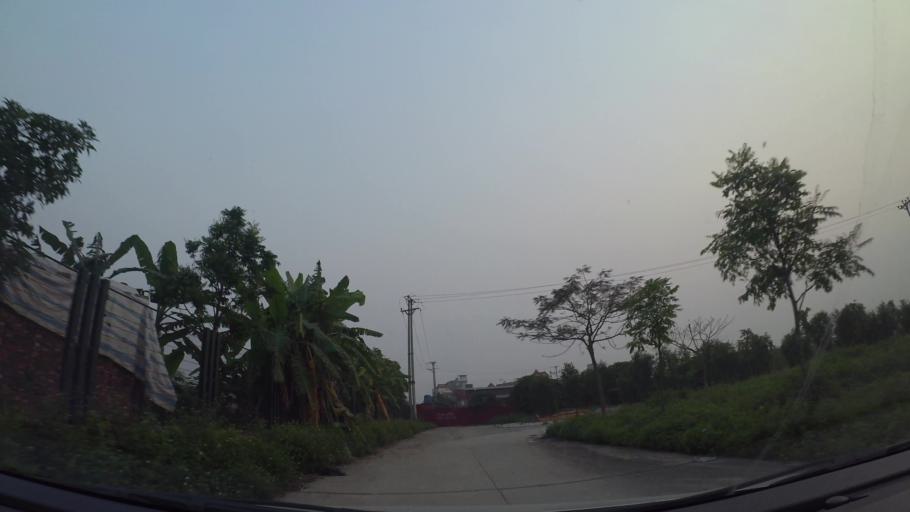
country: VN
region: Ha Noi
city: Ha Dong
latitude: 20.9943
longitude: 105.7341
